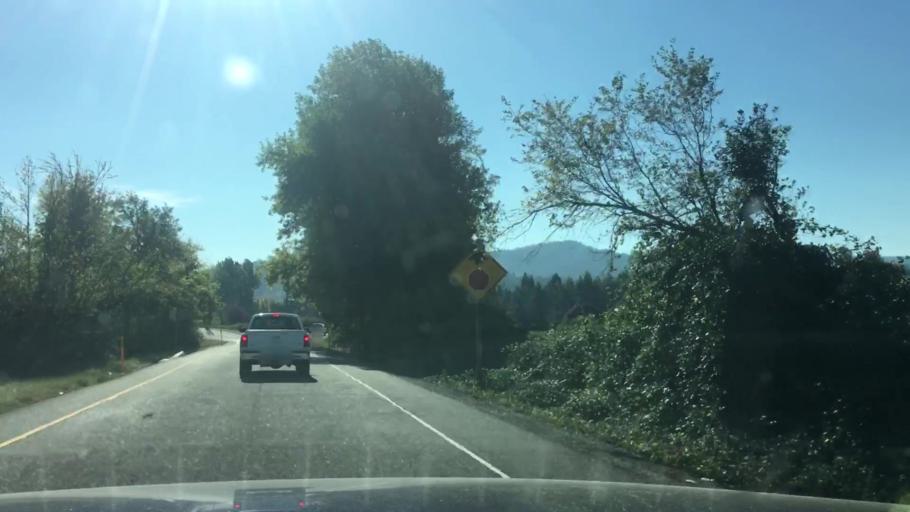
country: US
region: Oregon
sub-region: Lane County
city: Cottage Grove
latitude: 43.8334
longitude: -123.0308
